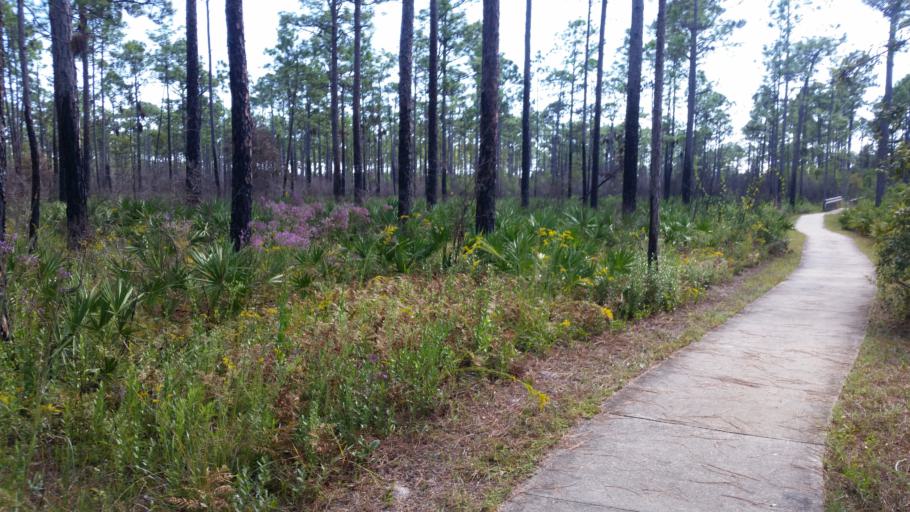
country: US
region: Florida
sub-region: Escambia County
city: Myrtle Grove
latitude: 30.3699
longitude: -87.4046
